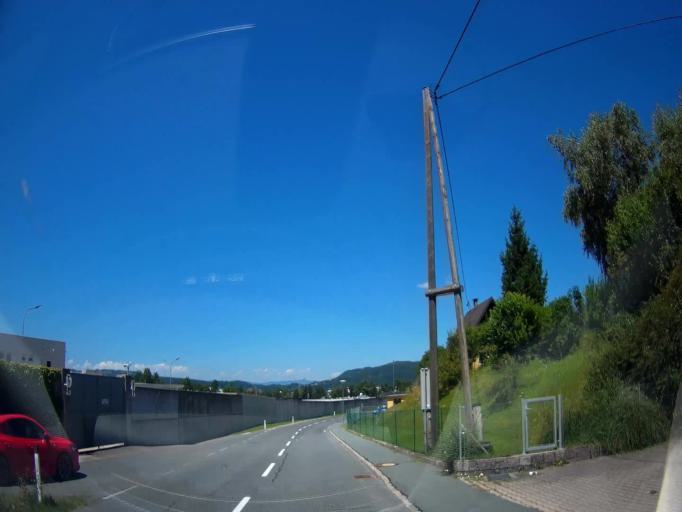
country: AT
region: Carinthia
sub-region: Politischer Bezirk Klagenfurt Land
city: Ferlach
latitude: 46.5209
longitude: 14.2977
